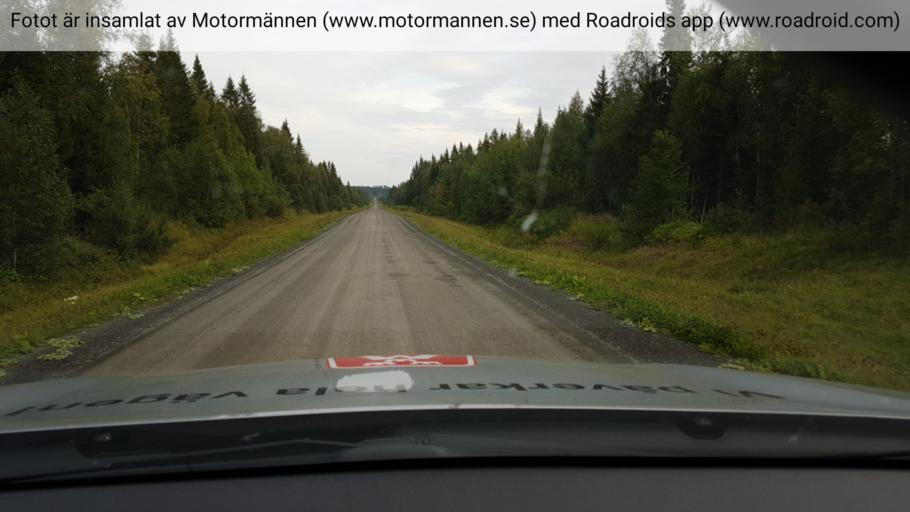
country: SE
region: Jaemtland
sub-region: OEstersunds Kommun
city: Lit
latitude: 63.6584
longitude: 14.9193
